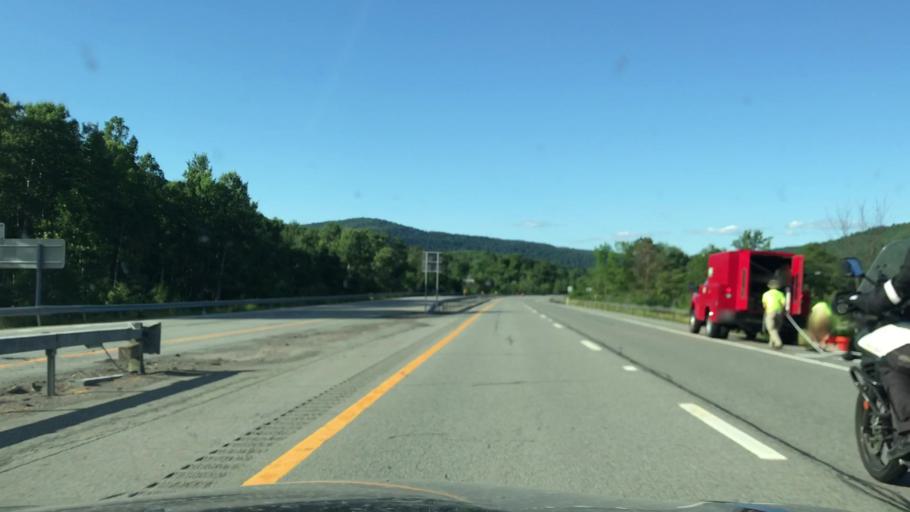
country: US
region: New York
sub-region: Delaware County
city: Hancock
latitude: 41.9736
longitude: -75.1757
